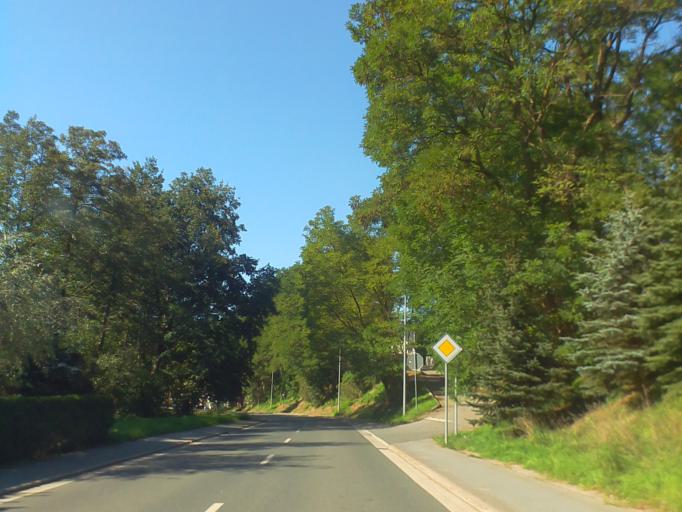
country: DE
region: Thuringia
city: Trobnitz
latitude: 50.8383
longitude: 11.7321
